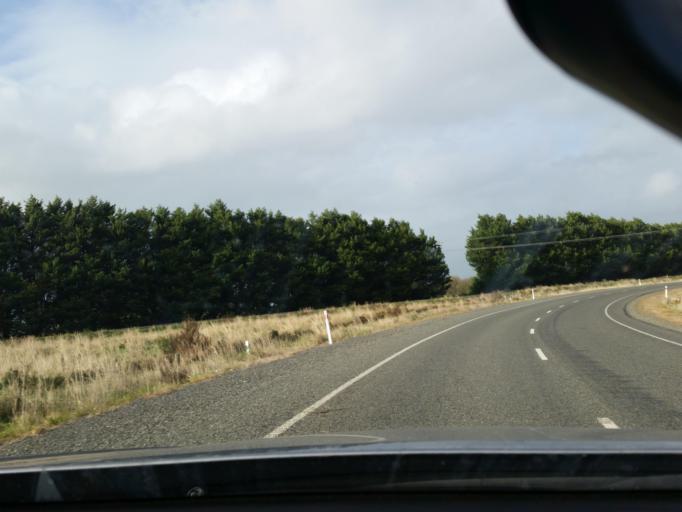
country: NZ
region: Southland
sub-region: Invercargill City
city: Invercargill
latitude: -46.3081
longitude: 168.3339
